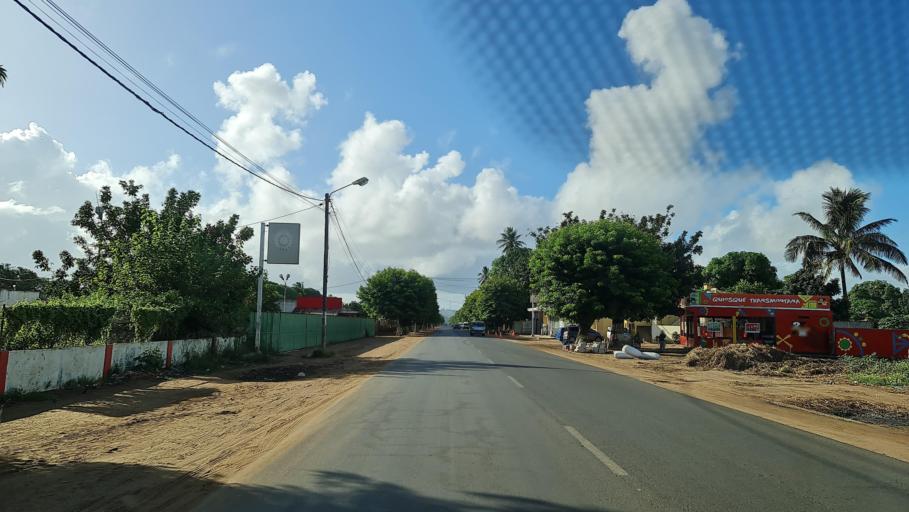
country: MZ
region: Gaza
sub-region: Xai-Xai District
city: Xai-Xai
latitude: -25.0326
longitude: 33.6348
